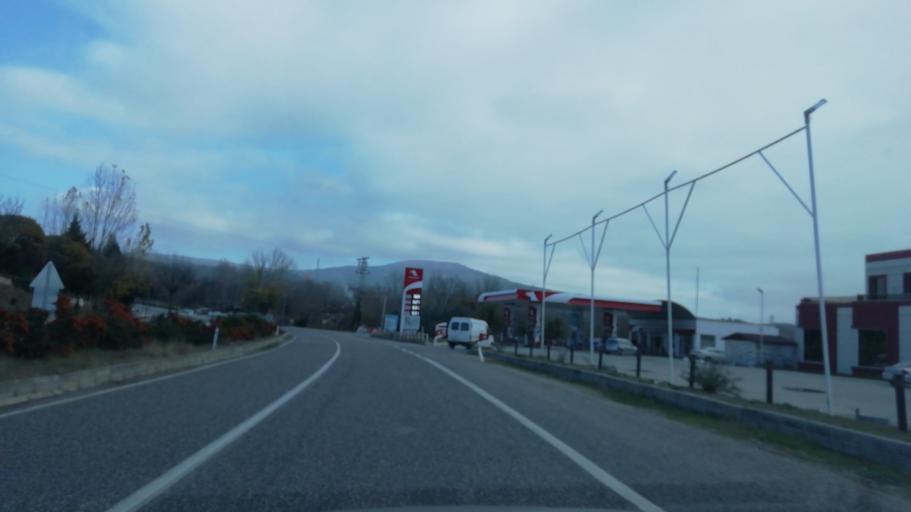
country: TR
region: Karabuk
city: Safranbolu
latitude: 41.2155
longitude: 32.7627
